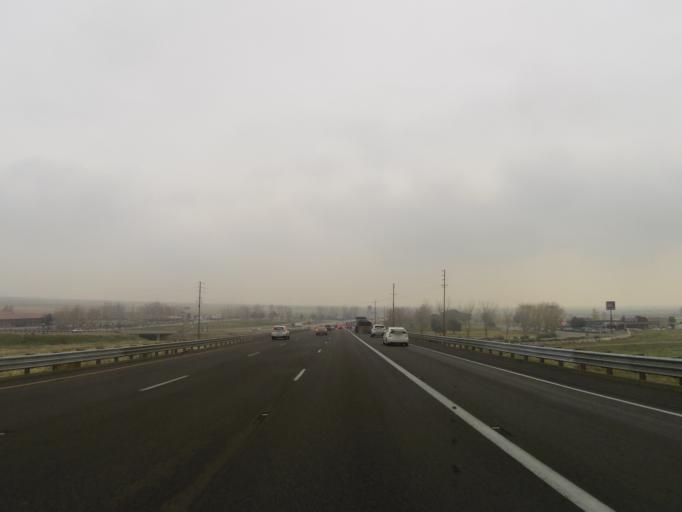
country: US
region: California
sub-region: Kern County
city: Lebec
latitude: 34.9376
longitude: -118.9285
